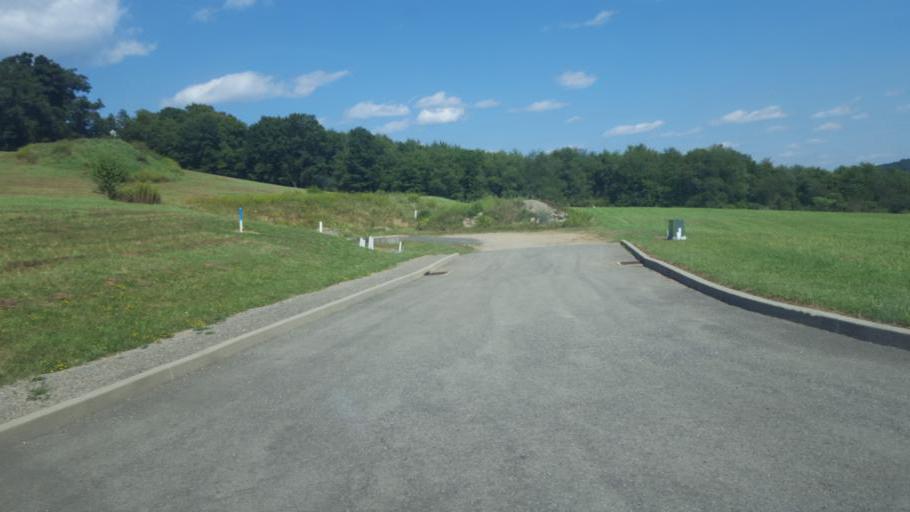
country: US
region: Pennsylvania
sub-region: Clarion County
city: Clarion
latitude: 41.1797
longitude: -79.3917
